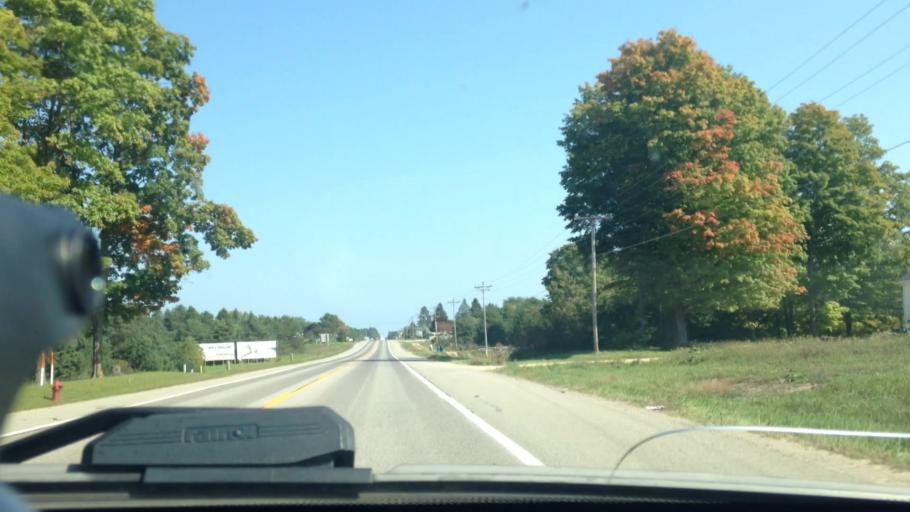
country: US
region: Michigan
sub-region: Luce County
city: Newberry
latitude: 46.3034
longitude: -85.5039
